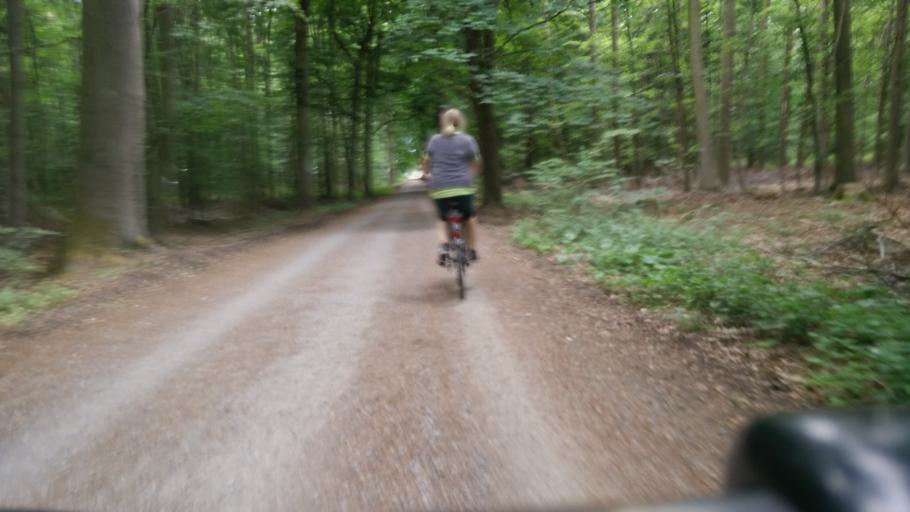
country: DE
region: Lower Saxony
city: Wunstorf
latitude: 52.4358
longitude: 9.4020
